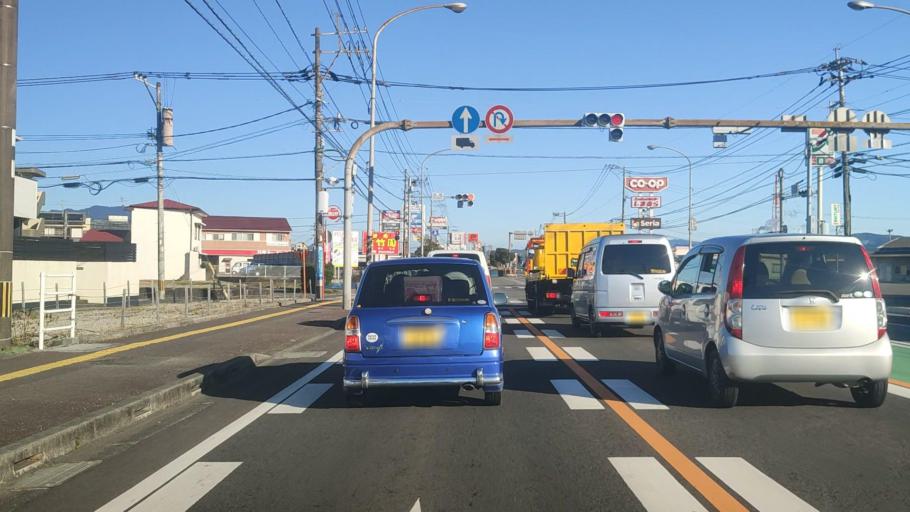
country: JP
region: Miyazaki
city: Nobeoka
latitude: 32.5583
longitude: 131.6802
